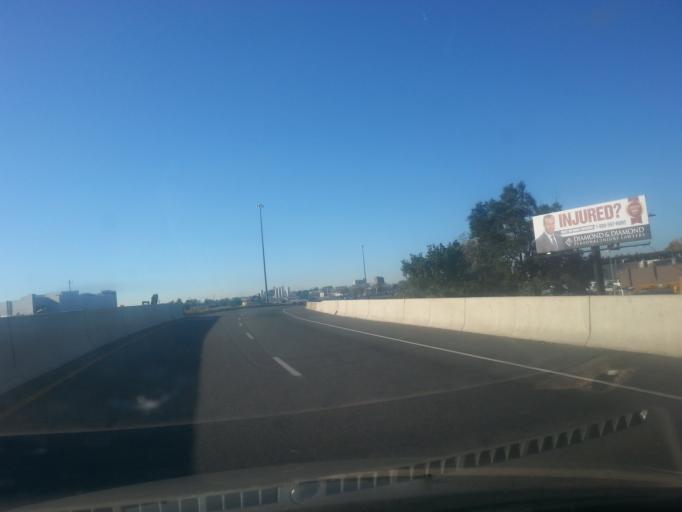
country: CA
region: Ontario
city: Etobicoke
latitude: 43.7186
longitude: -79.5191
